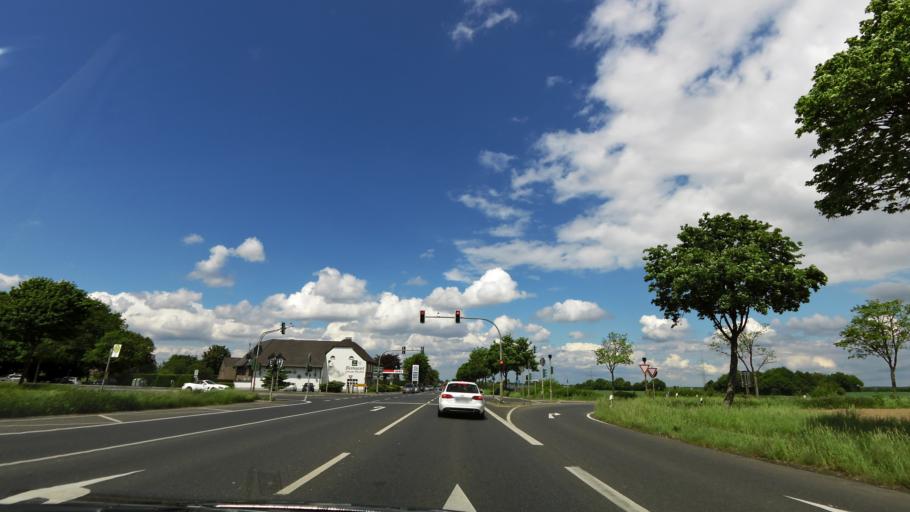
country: DE
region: North Rhine-Westphalia
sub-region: Regierungsbezirk Koln
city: Heinsberg
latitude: 51.0294
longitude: 6.1086
